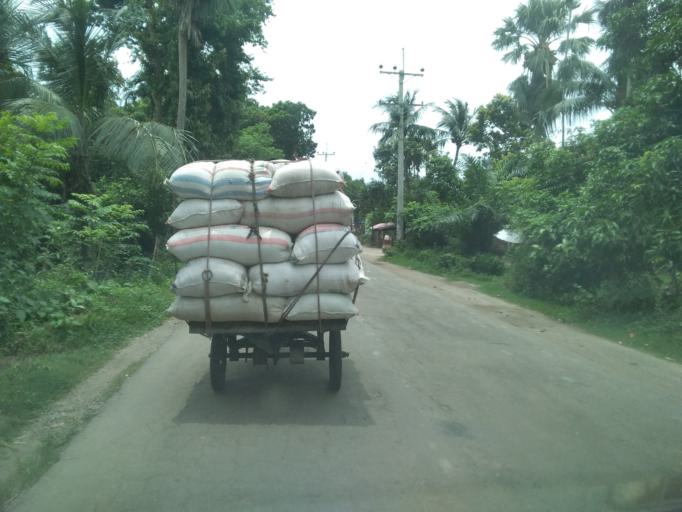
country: IN
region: West Bengal
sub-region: North 24 Parganas
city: Taki
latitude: 22.5725
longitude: 89.0004
